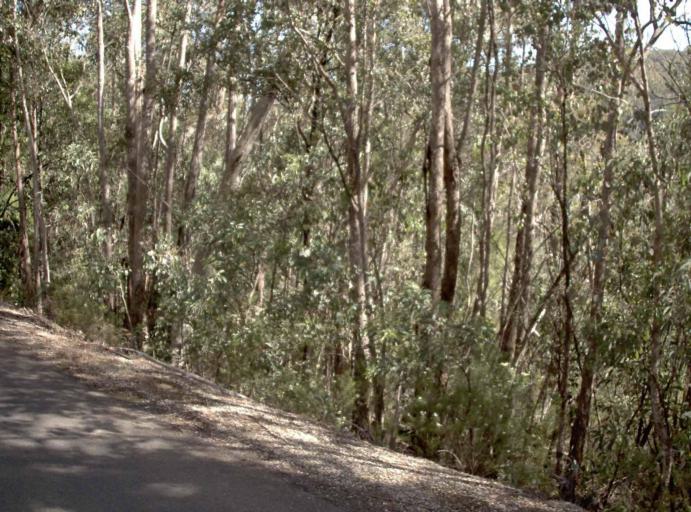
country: AU
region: Victoria
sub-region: East Gippsland
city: Lakes Entrance
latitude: -37.4203
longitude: 148.1271
